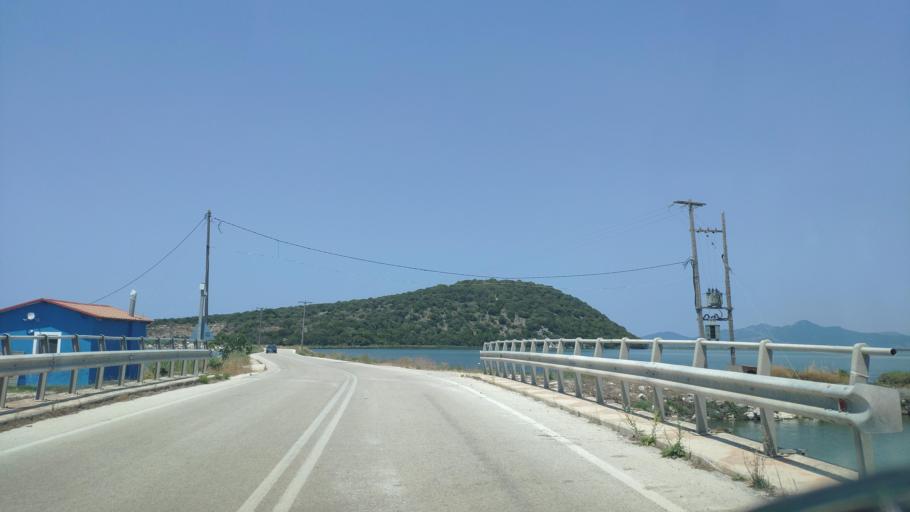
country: GR
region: Epirus
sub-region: Nomos Artas
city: Aneza
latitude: 39.0353
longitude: 20.8787
